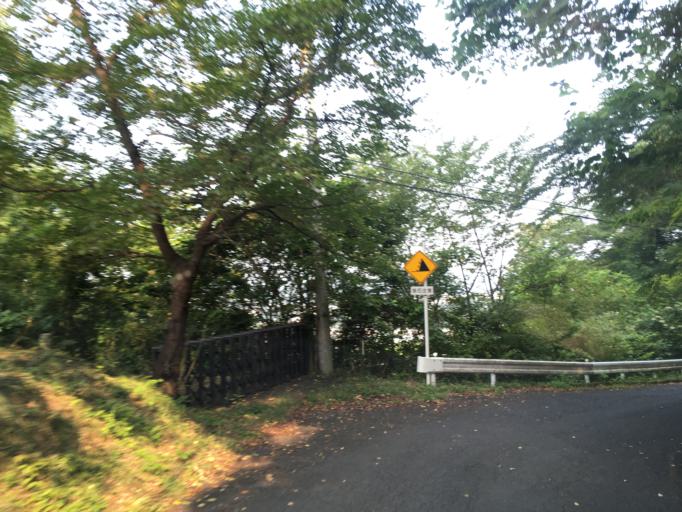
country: JP
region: Saitama
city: Chichibu
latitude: 35.9841
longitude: 139.1141
